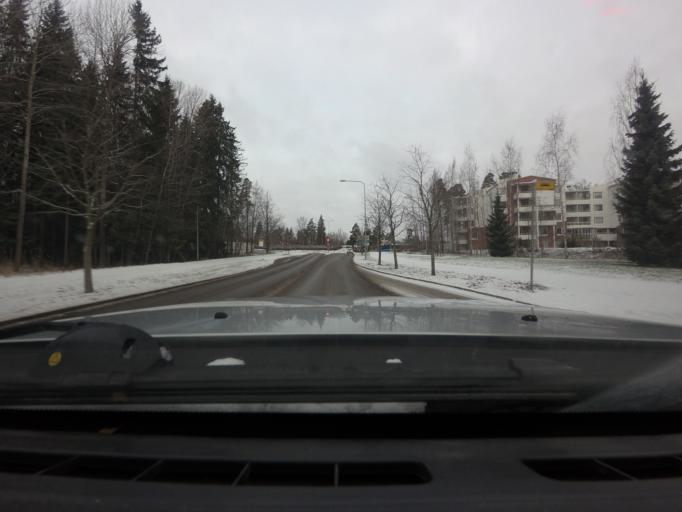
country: FI
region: Uusimaa
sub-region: Helsinki
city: Kilo
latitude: 60.2100
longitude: 24.7627
